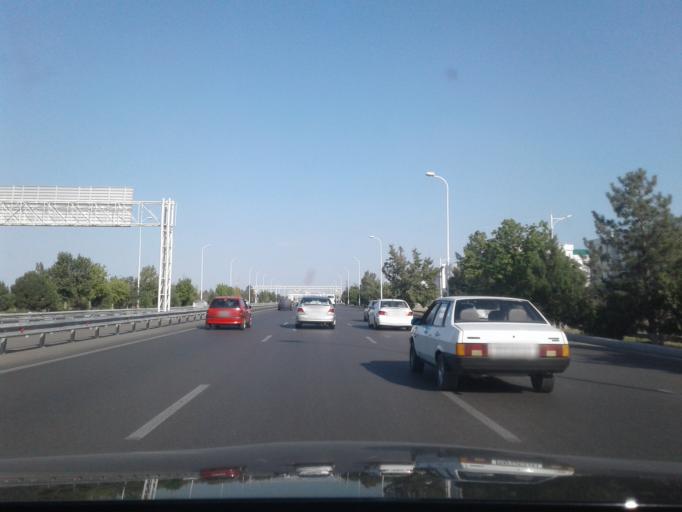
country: TM
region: Ahal
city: Ashgabat
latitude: 37.9845
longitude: 58.3300
